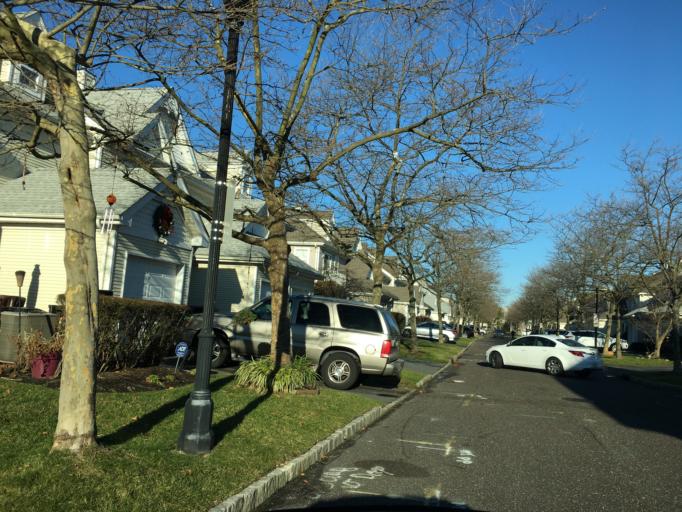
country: US
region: New Jersey
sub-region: Atlantic County
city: Atlantic City
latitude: 39.3730
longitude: -74.4189
